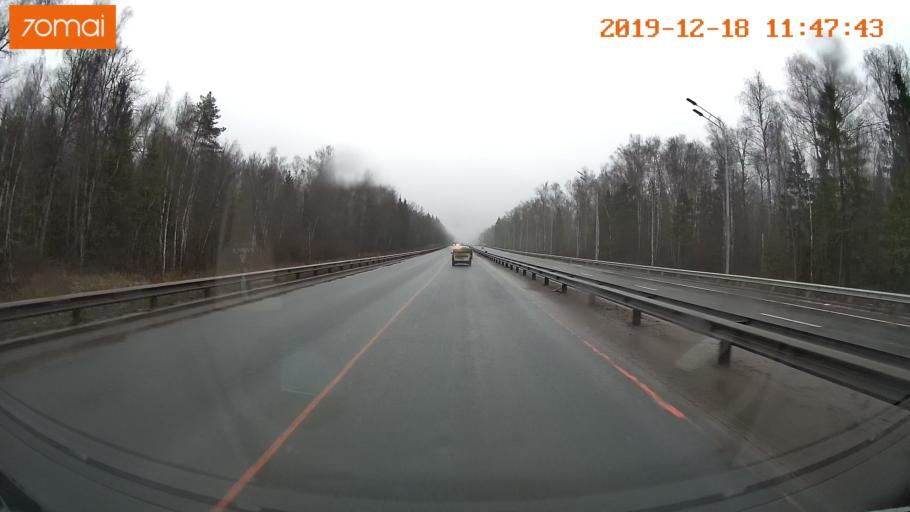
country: RU
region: Moskovskaya
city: Yershovo
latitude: 55.7607
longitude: 36.8971
